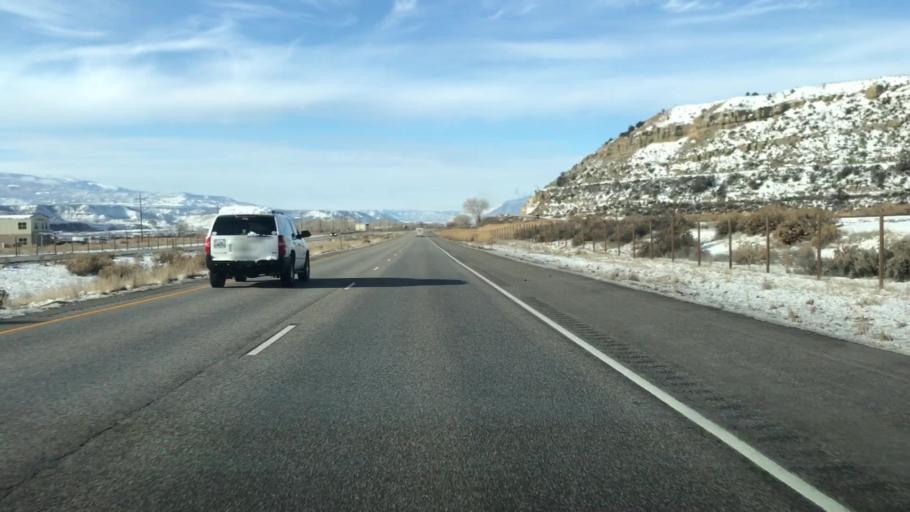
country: US
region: Colorado
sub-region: Garfield County
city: Silt
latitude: 39.5469
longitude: -107.6205
